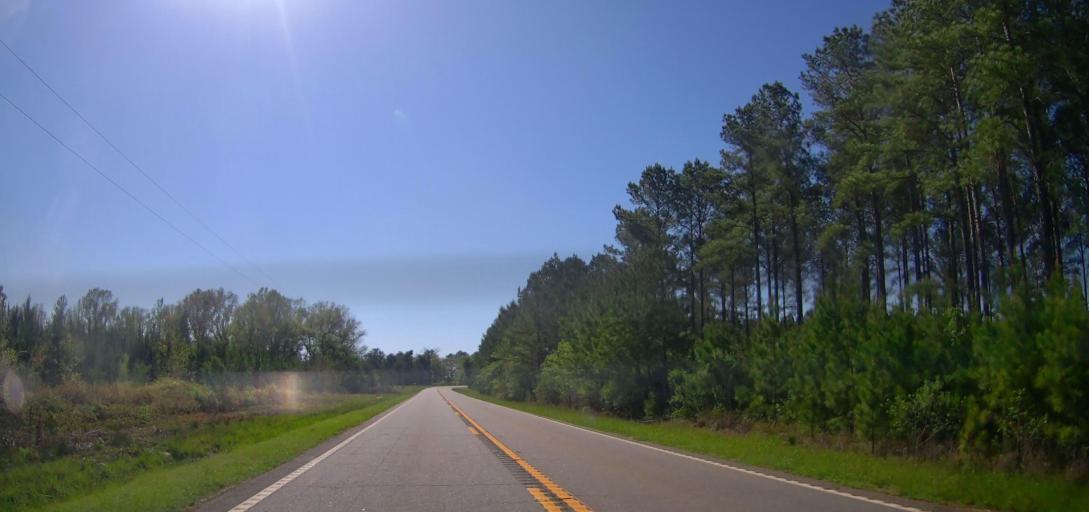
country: US
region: Georgia
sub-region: Dooly County
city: Unadilla
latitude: 32.2553
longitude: -83.6431
